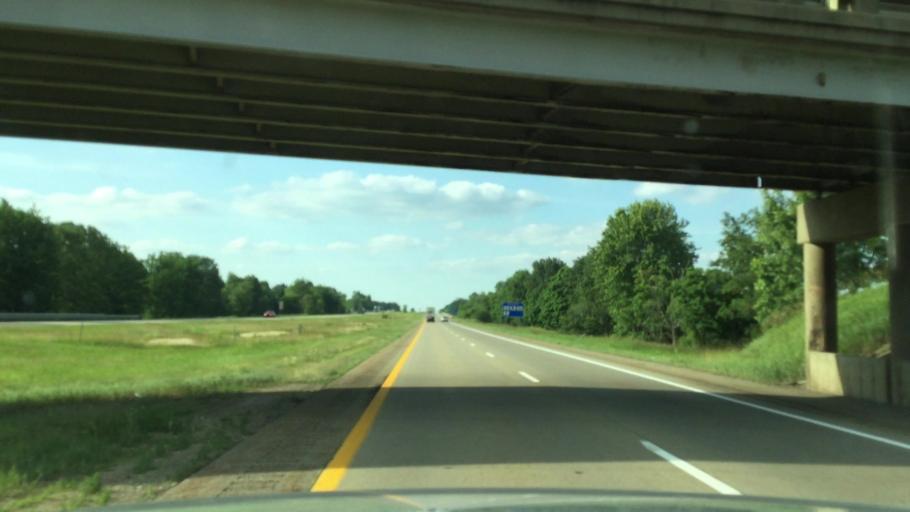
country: US
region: Michigan
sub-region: Branch County
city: Union City
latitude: 42.0918
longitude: -84.9974
